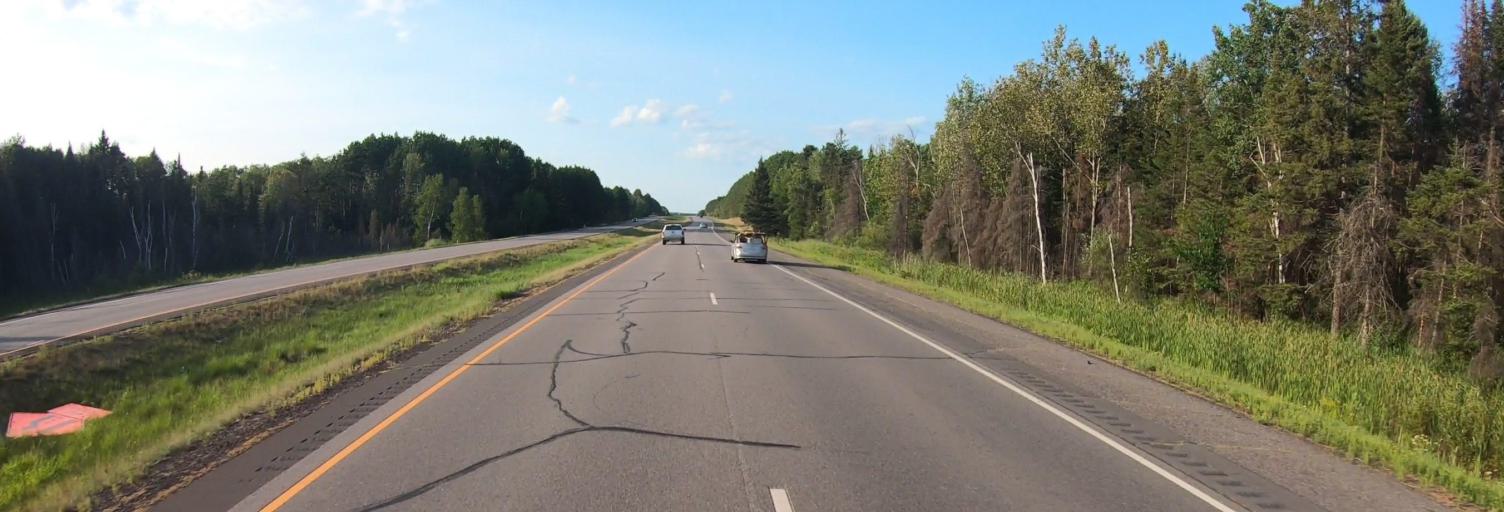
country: US
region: Minnesota
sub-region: Saint Louis County
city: Eveleth
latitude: 47.4099
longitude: -92.5208
